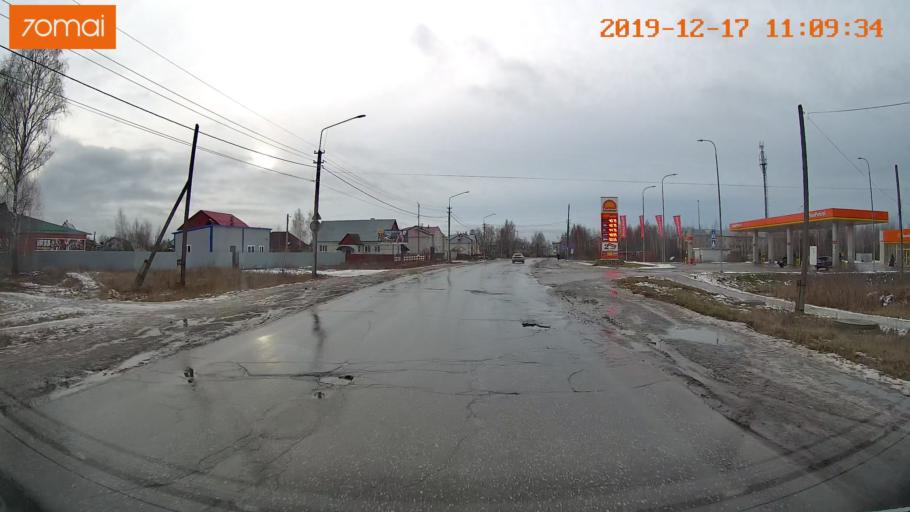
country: RU
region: Vladimir
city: Gus'-Khrustal'nyy
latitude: 55.5994
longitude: 40.6423
